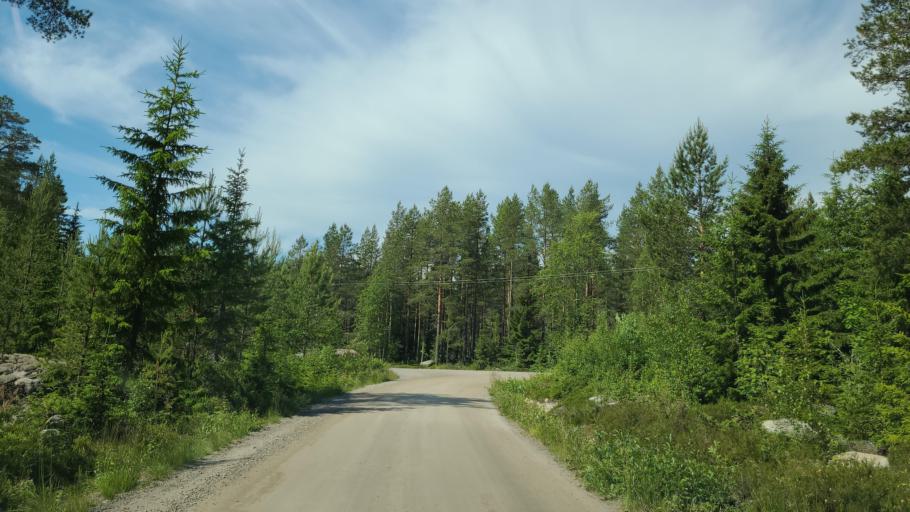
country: SE
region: Vaesterbotten
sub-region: Robertsfors Kommun
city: Robertsfors
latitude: 64.1574
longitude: 20.9404
